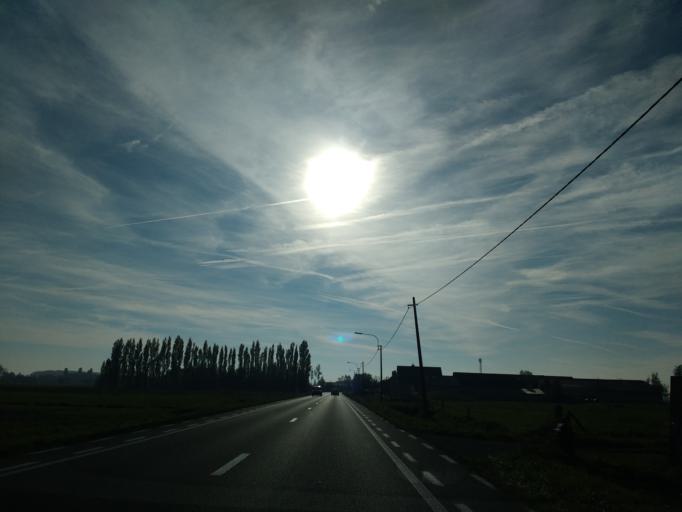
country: BE
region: Flanders
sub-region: Provincie Oost-Vlaanderen
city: Kaprijke
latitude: 51.2337
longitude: 3.6184
